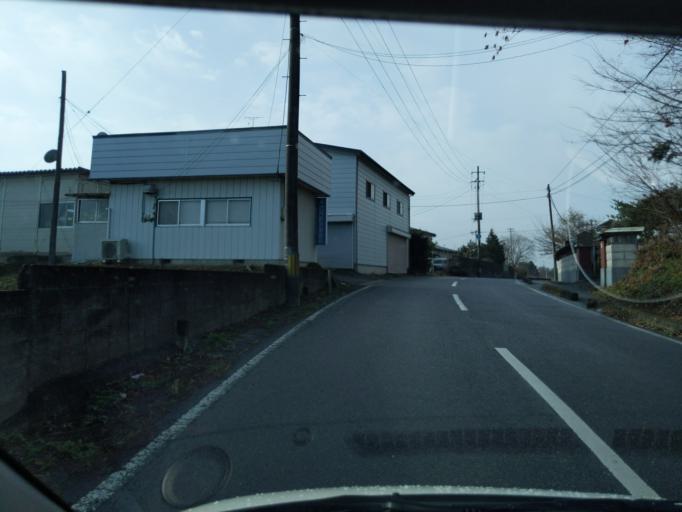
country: JP
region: Miyagi
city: Wakuya
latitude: 38.7002
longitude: 141.1588
